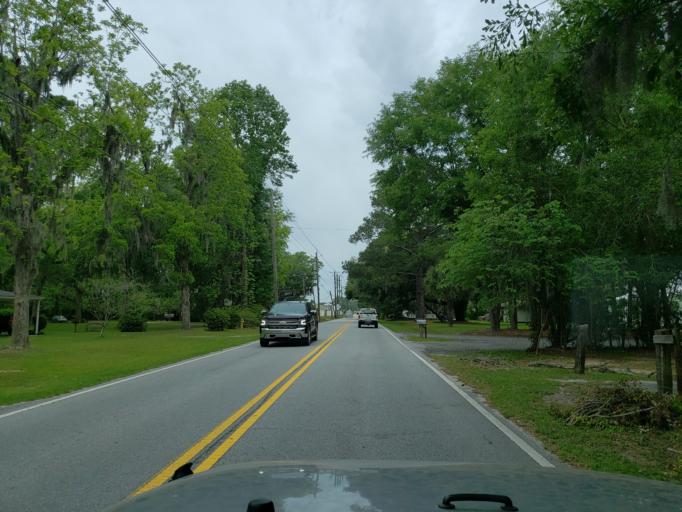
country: US
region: Georgia
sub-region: Chatham County
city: Port Wentworth
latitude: 32.1833
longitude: -81.2147
